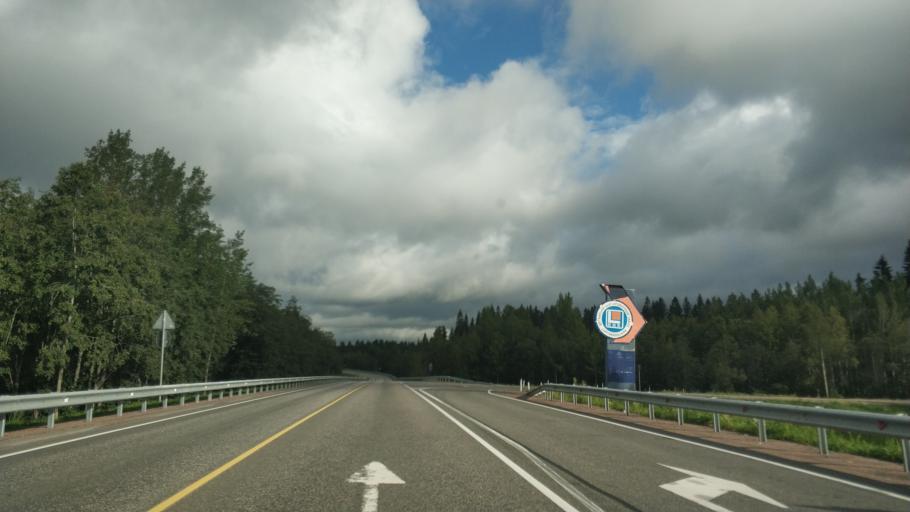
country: RU
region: Republic of Karelia
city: Khelyulya
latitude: 61.7800
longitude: 30.6589
